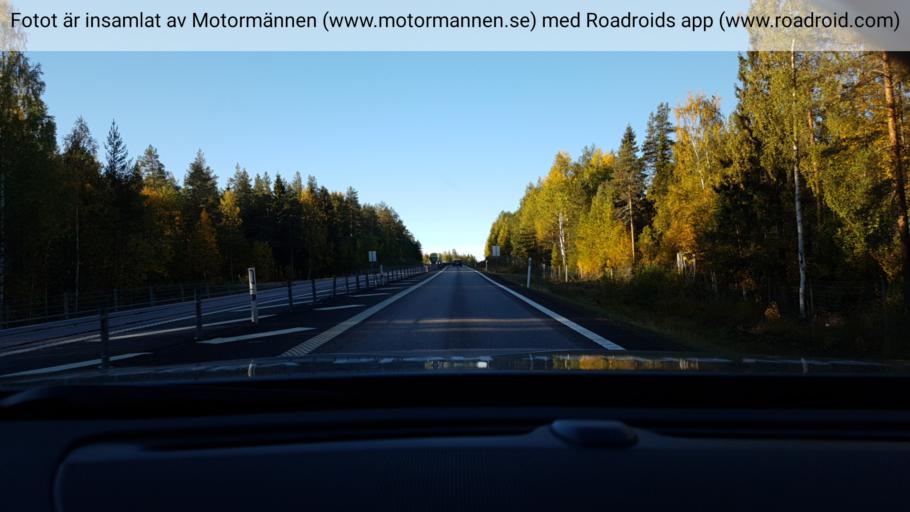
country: SE
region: Norrbotten
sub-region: Pitea Kommun
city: Rosvik
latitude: 65.4678
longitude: 21.7142
